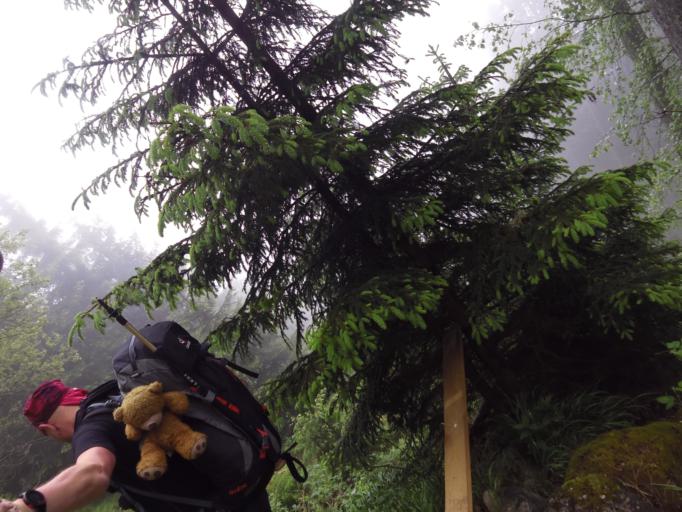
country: AT
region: Tyrol
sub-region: Politischer Bezirk Innsbruck Land
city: Neustift im Stubaital
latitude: 47.0509
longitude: 11.2247
